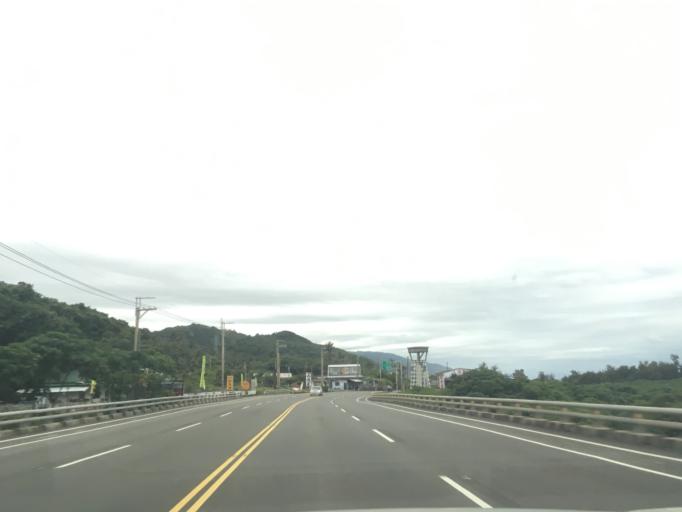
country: TW
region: Taiwan
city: Hengchun
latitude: 22.3022
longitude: 120.8889
